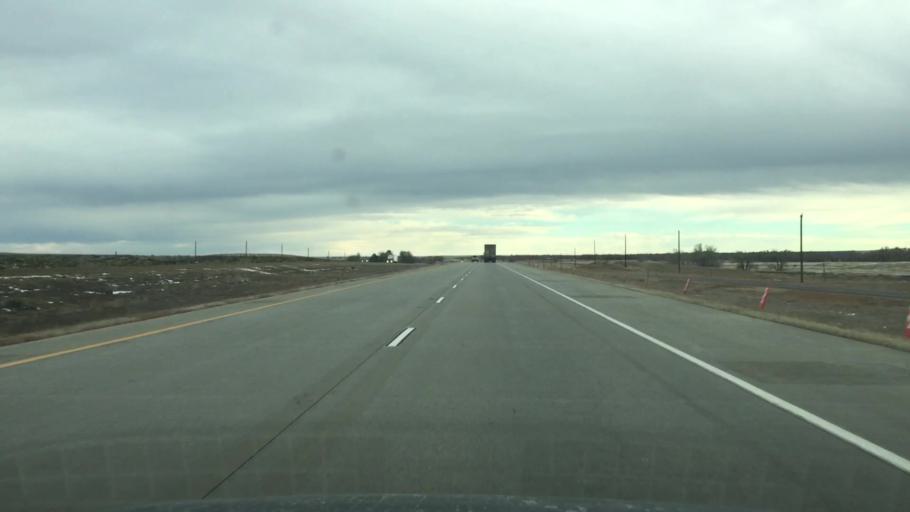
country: US
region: Colorado
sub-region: Arapahoe County
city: Byers
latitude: 39.5269
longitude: -103.9876
